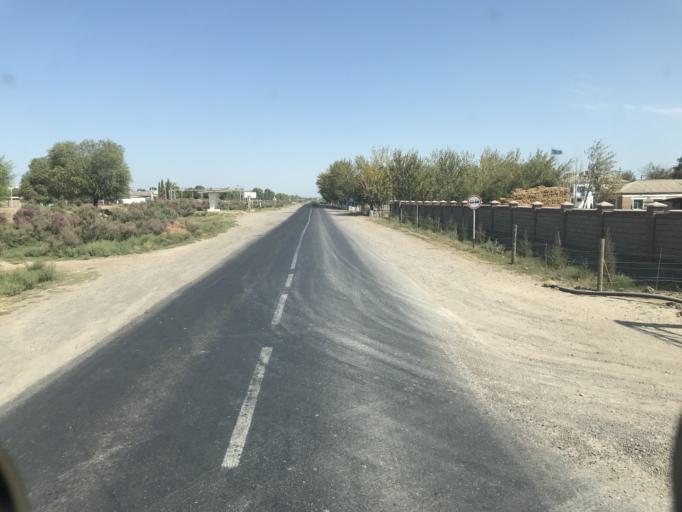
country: KZ
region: Ongtustik Qazaqstan
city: Ilyich
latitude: 40.7686
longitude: 68.5373
